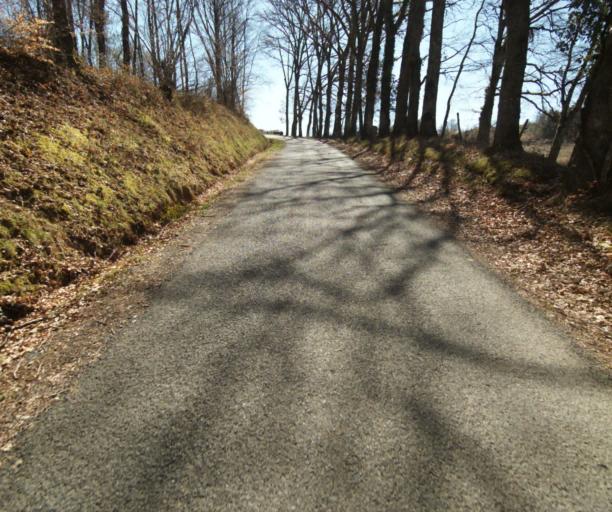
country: FR
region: Limousin
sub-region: Departement de la Correze
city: Chamboulive
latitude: 45.4410
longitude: 1.7003
